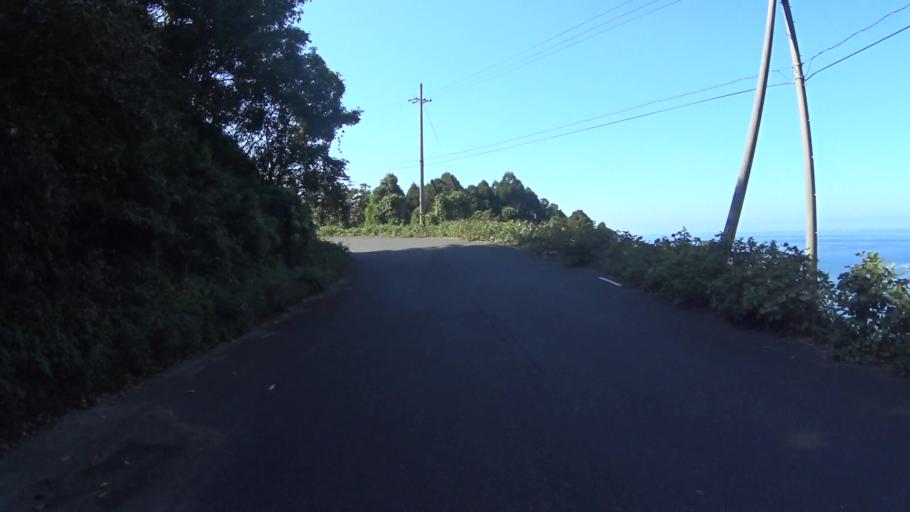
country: JP
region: Kyoto
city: Miyazu
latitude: 35.7705
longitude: 135.2228
